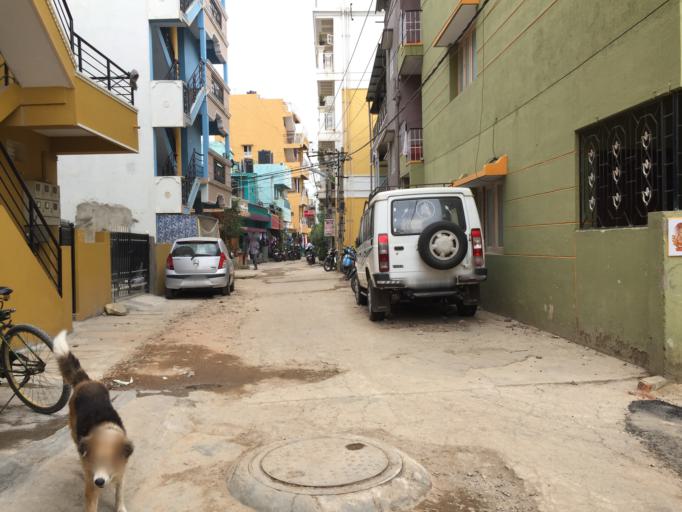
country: IN
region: Karnataka
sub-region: Bangalore Urban
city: Bangalore
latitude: 12.9568
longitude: 77.6567
